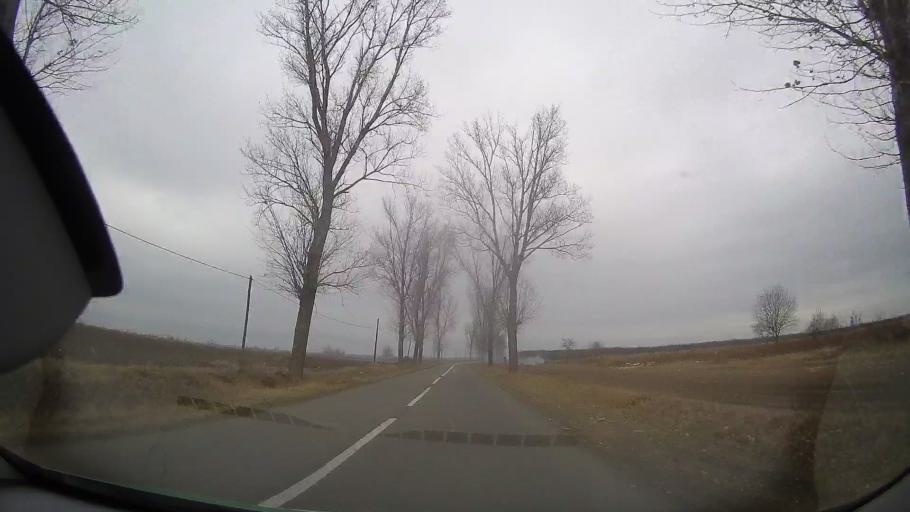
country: RO
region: Braila
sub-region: Comuna Rosiori
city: Rosiori
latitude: 44.8168
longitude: 27.3935
